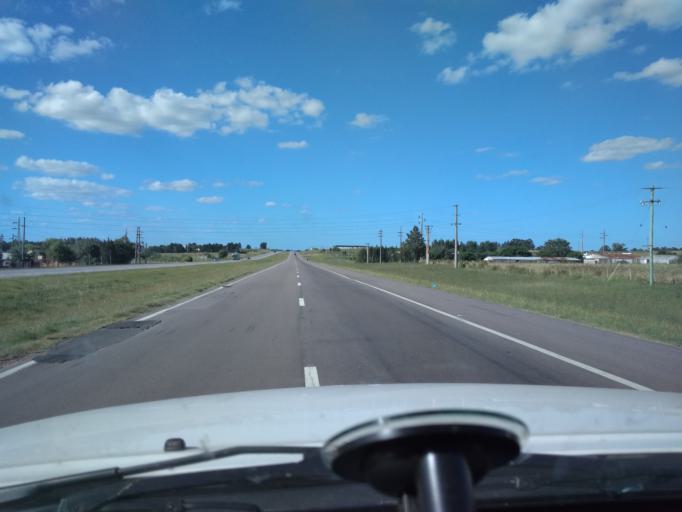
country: UY
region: Canelones
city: Las Piedras
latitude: -34.7139
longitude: -56.2435
